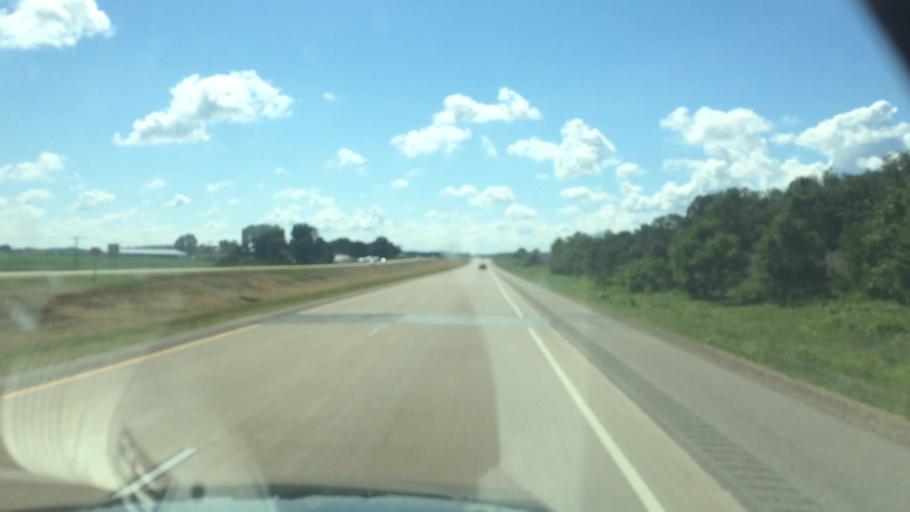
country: US
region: Wisconsin
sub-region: Portage County
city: Amherst
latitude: 44.4979
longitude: -89.3737
